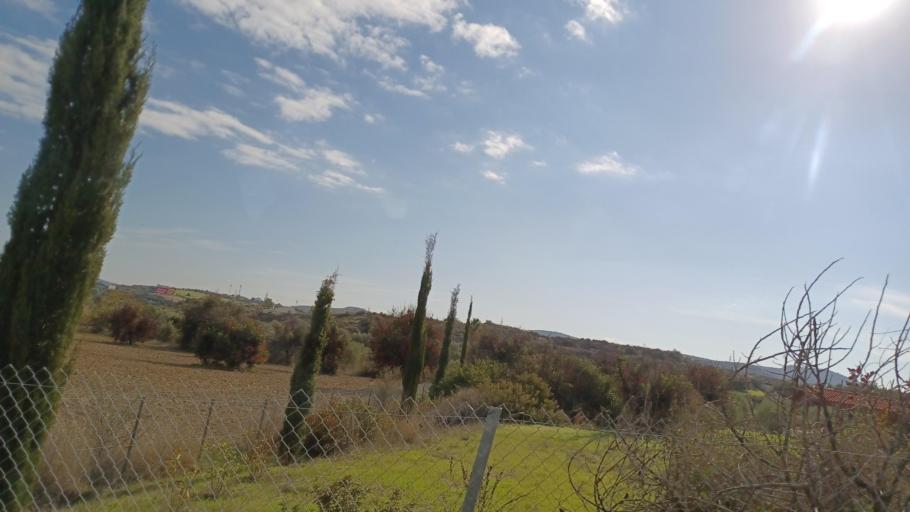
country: CY
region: Larnaka
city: Kofinou
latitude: 34.8158
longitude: 33.3472
